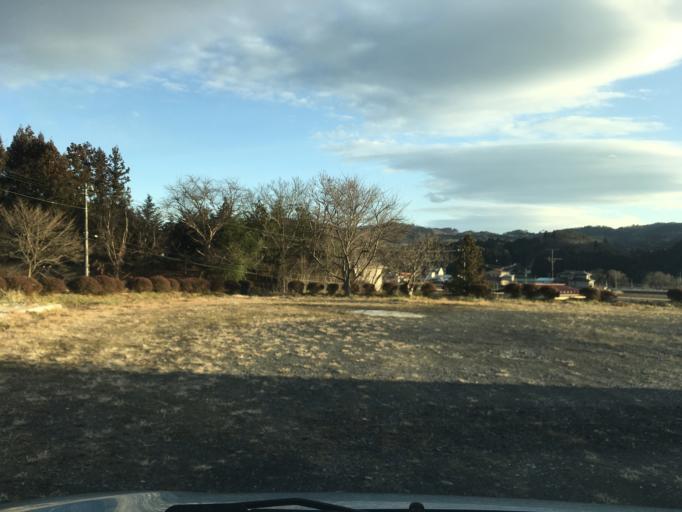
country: JP
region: Iwate
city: Ichinoseki
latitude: 38.8522
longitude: 141.2913
